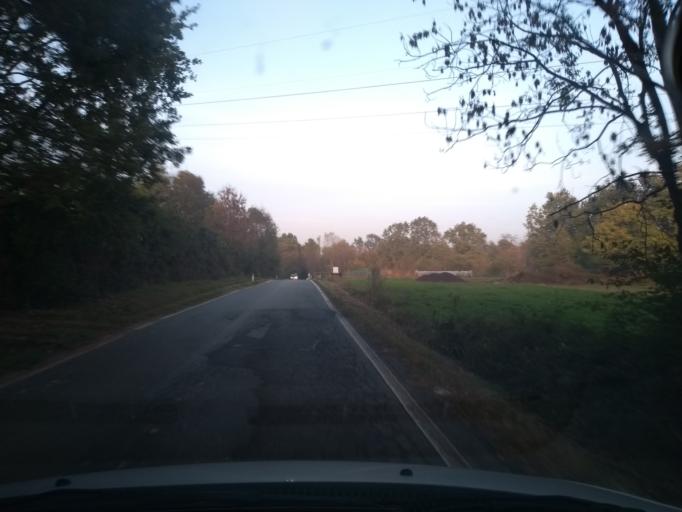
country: IT
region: Piedmont
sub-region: Provincia di Torino
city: La Cassa
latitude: 45.1750
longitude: 7.5114
